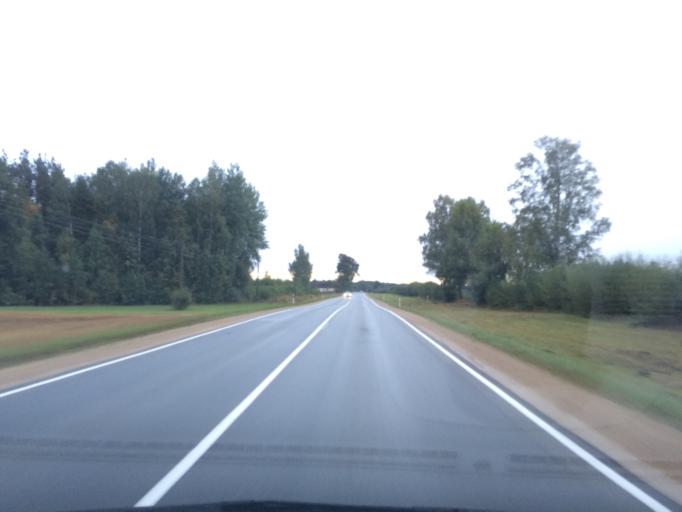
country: LV
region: Salas
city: Sala
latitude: 56.5641
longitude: 25.7760
